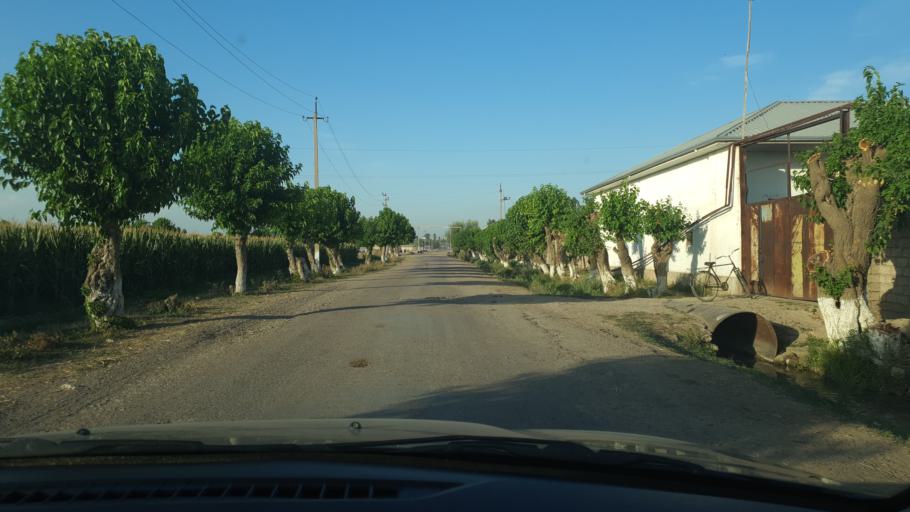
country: UZ
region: Toshkent
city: Tuytepa
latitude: 41.1019
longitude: 69.3845
